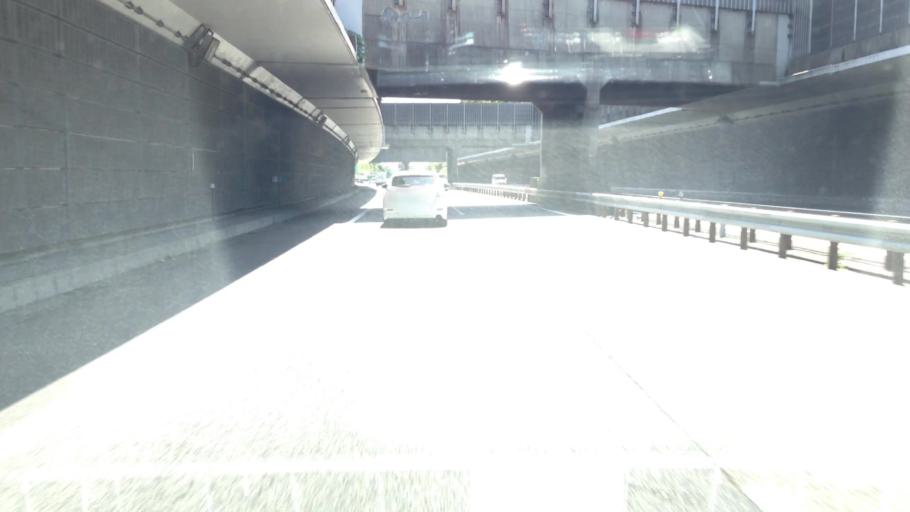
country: JP
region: Kanagawa
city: Yokohama
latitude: 35.4338
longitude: 139.5818
